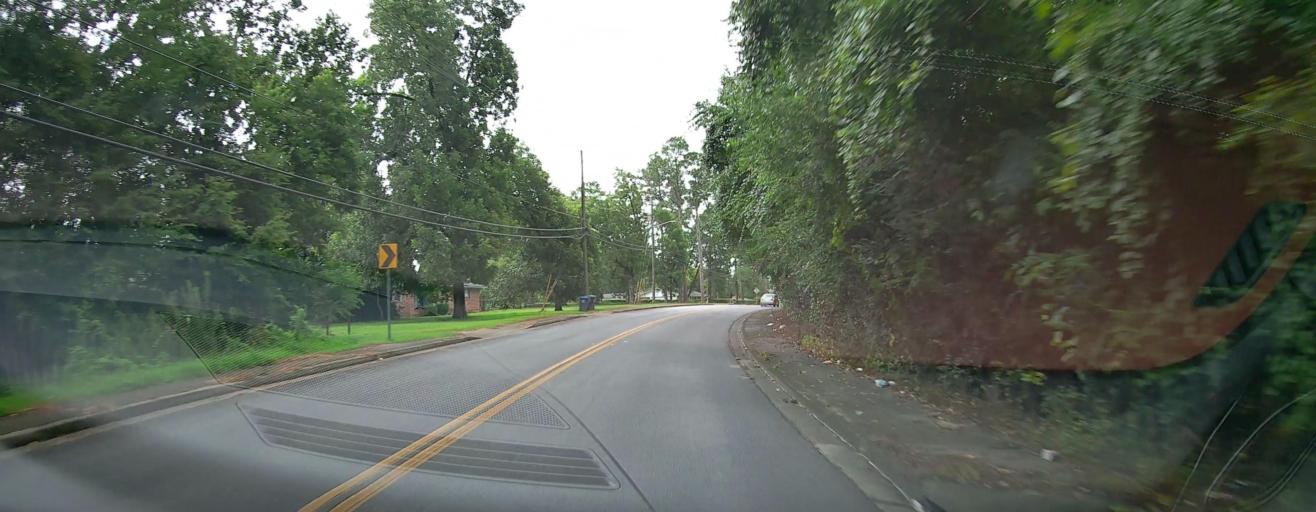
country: US
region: Georgia
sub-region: Bibb County
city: Macon
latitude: 32.7896
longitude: -83.6884
